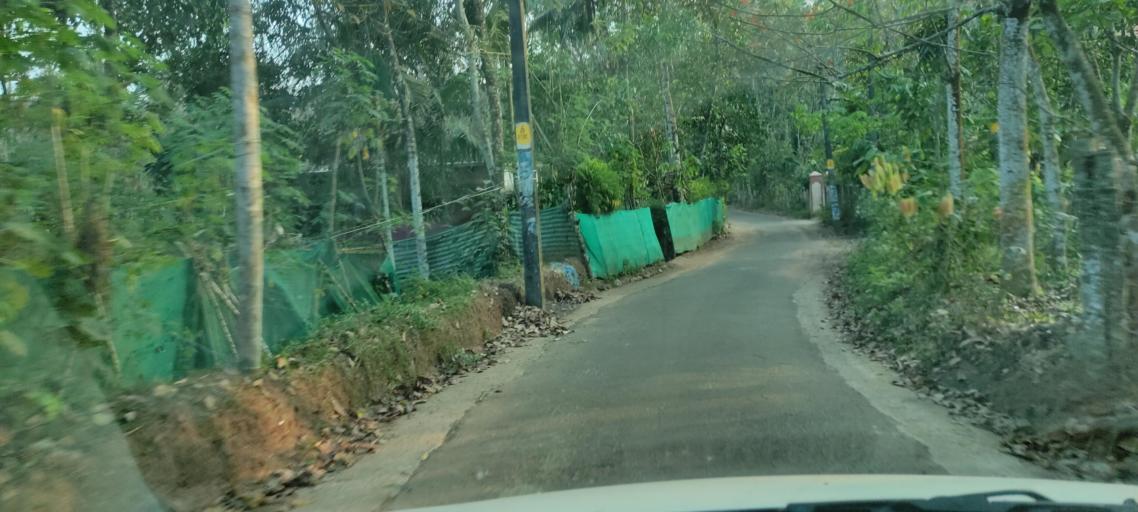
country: IN
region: Kerala
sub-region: Alappuzha
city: Kattanam
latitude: 9.1653
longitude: 76.5904
